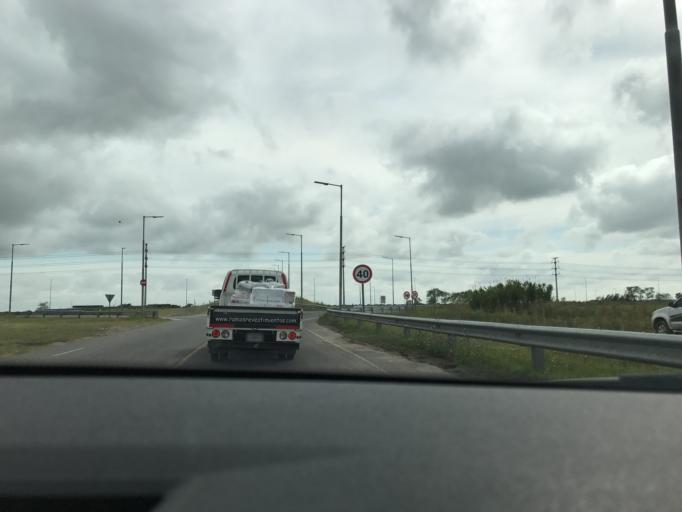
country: AR
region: Buenos Aires
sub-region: Partido de La Plata
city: La Plata
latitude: -34.8409
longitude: -58.0719
